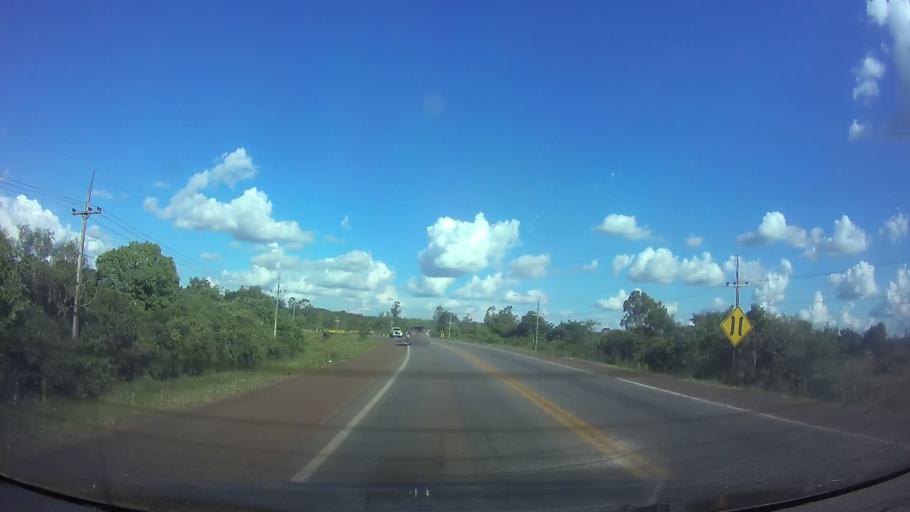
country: PY
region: Cordillera
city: Eusebio Ayala
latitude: -25.3903
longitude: -56.9661
